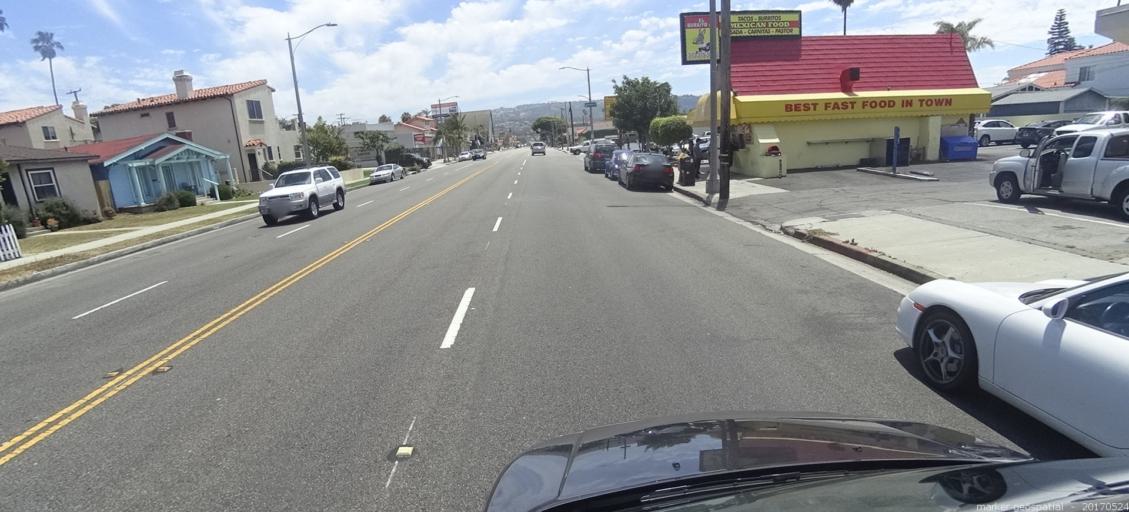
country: US
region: California
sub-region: Los Angeles County
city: Redondo Beach
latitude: 33.8275
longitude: -118.3858
